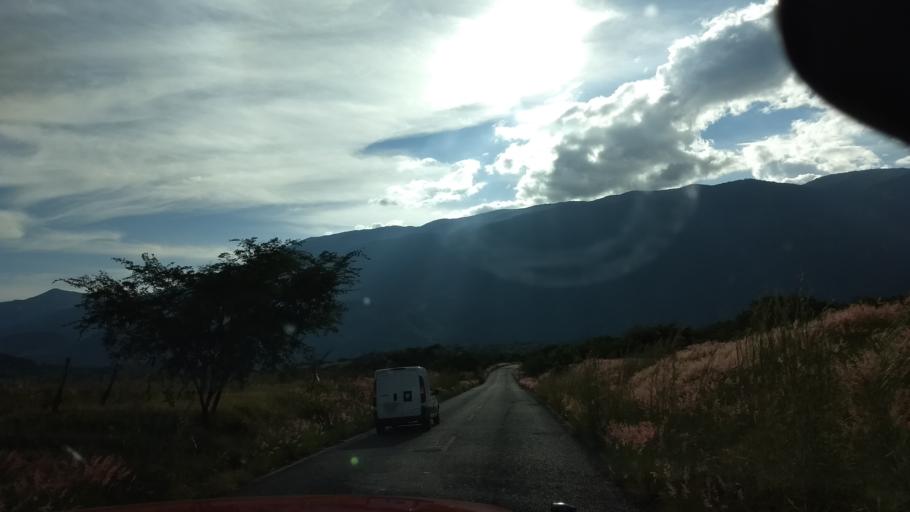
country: MX
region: Colima
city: Suchitlan
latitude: 19.4539
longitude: -103.8064
